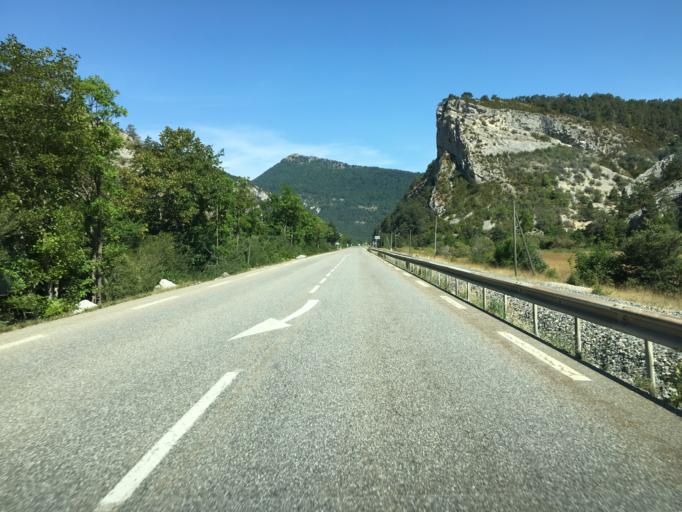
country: FR
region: Provence-Alpes-Cote d'Azur
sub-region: Departement des Hautes-Alpes
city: Veynes
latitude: 44.6243
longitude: 5.6986
